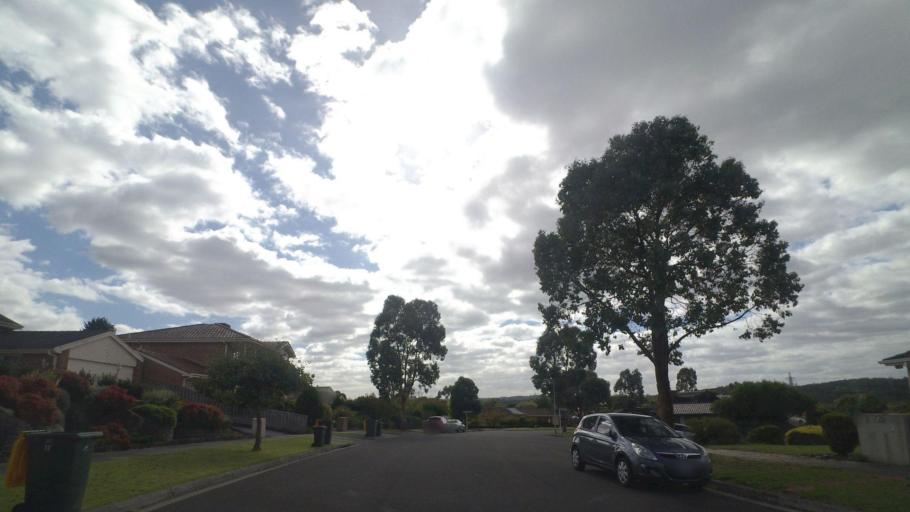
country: AU
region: Victoria
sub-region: Manningham
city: Donvale
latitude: -37.7606
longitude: 145.1772
